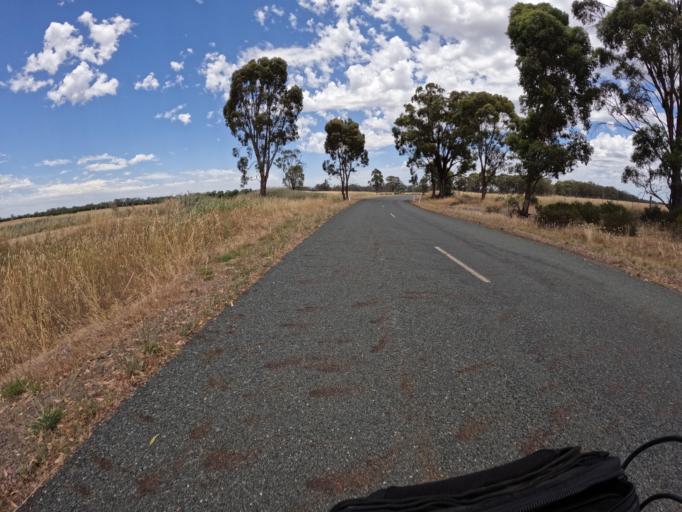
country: AU
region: Victoria
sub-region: Greater Shepparton
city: Shepparton
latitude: -36.6770
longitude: 145.1971
